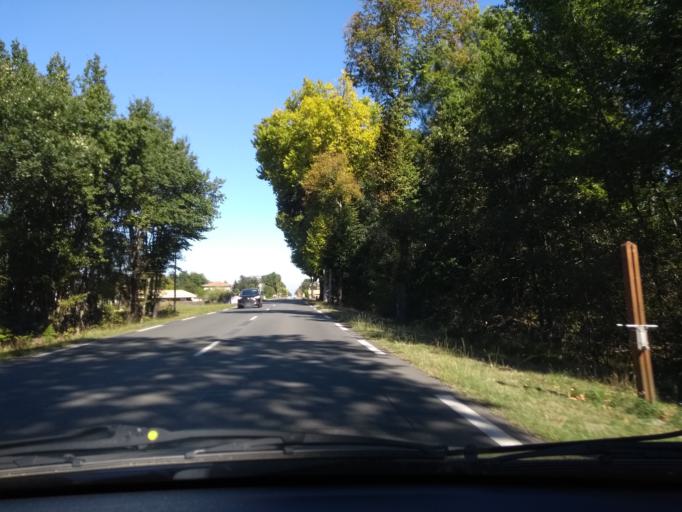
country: FR
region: Aquitaine
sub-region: Departement de la Gironde
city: Le Barp
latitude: 44.5702
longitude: -0.7807
